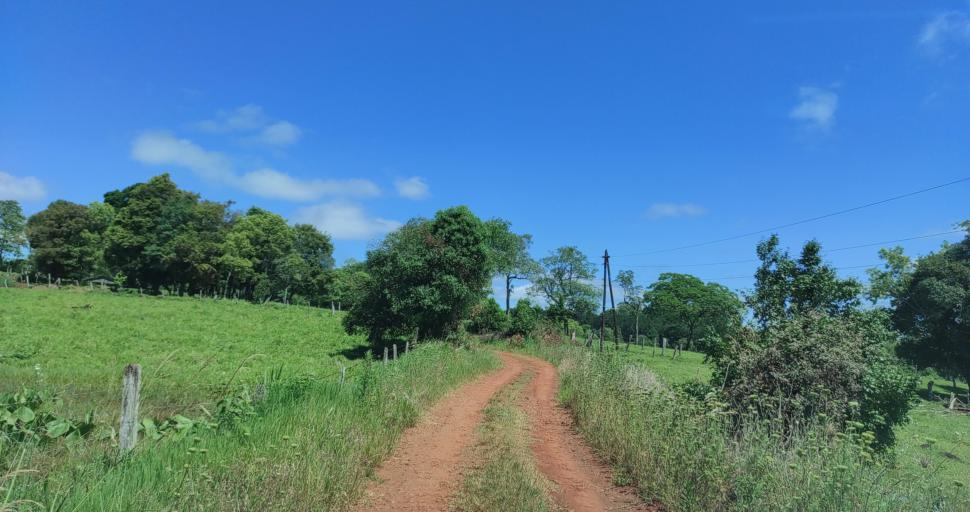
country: AR
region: Misiones
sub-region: Departamento de Veinticinco de Mayo
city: Veinticinco de Mayo
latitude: -27.4149
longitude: -54.7257
